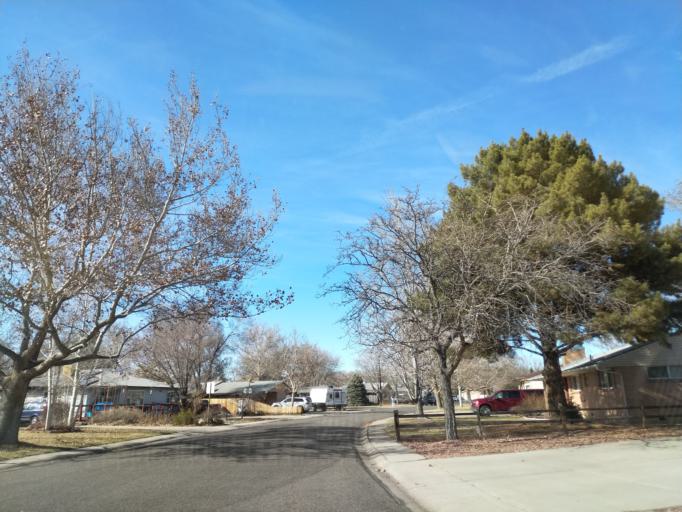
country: US
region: Colorado
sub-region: Mesa County
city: Grand Junction
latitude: 39.0829
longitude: -108.5672
